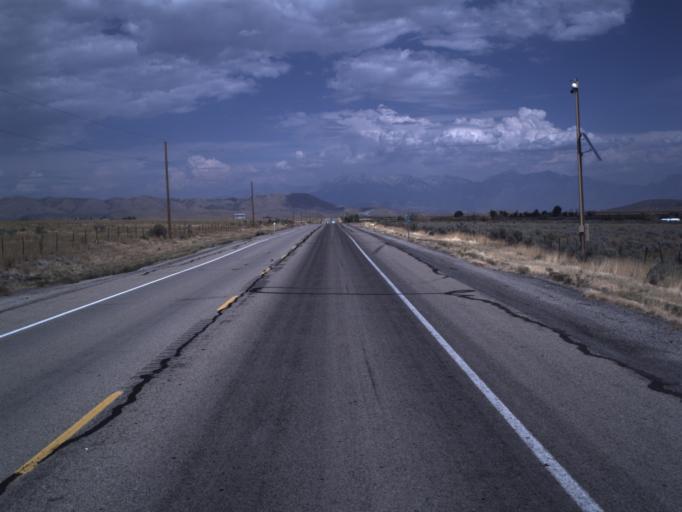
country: US
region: Utah
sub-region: Utah County
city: Eagle Mountain
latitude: 40.3352
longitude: -112.0977
